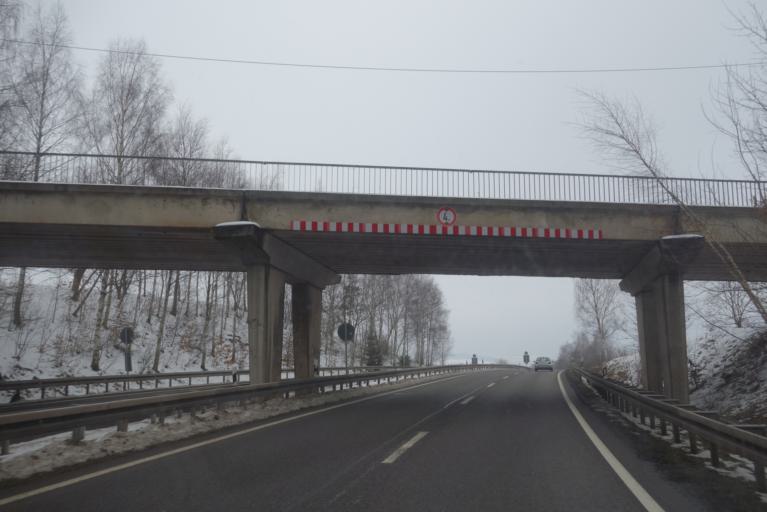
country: DE
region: Saxony
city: Niederwiesa
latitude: 50.8617
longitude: 13.0342
